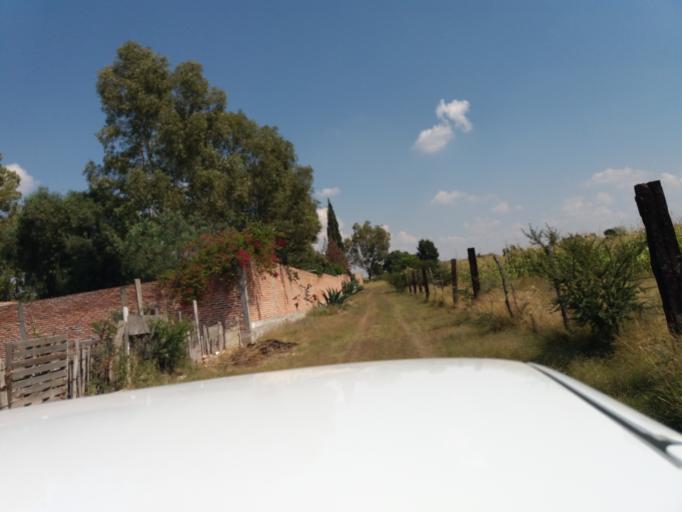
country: MX
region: Aguascalientes
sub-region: Aguascalientes
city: Penuelas (El Cienegal)
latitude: 21.7512
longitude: -102.3057
